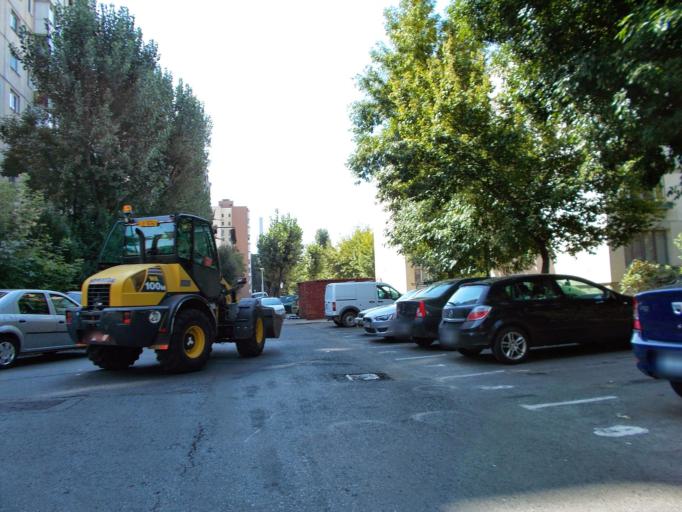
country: RO
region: Bucuresti
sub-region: Municipiul Bucuresti
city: Bucuresti
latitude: 44.3861
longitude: 26.1093
